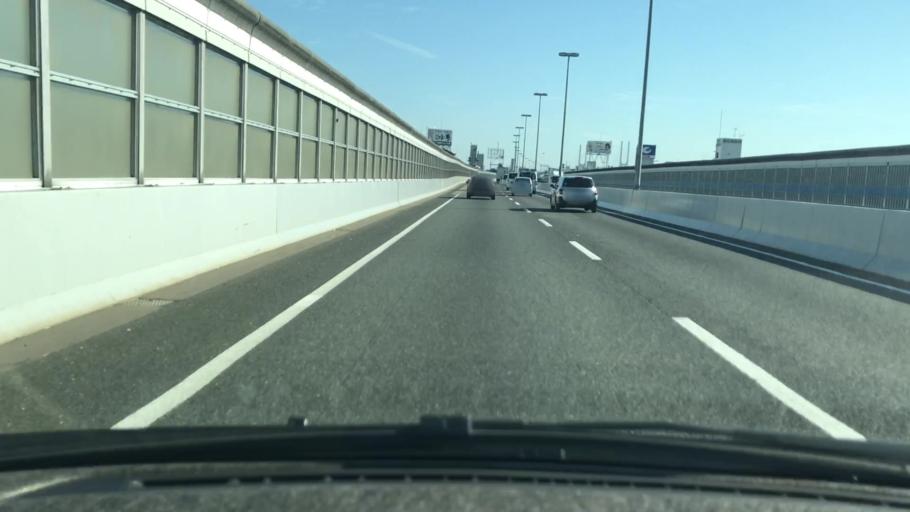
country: JP
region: Hyogo
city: Ashiya
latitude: 34.7112
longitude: 135.2552
